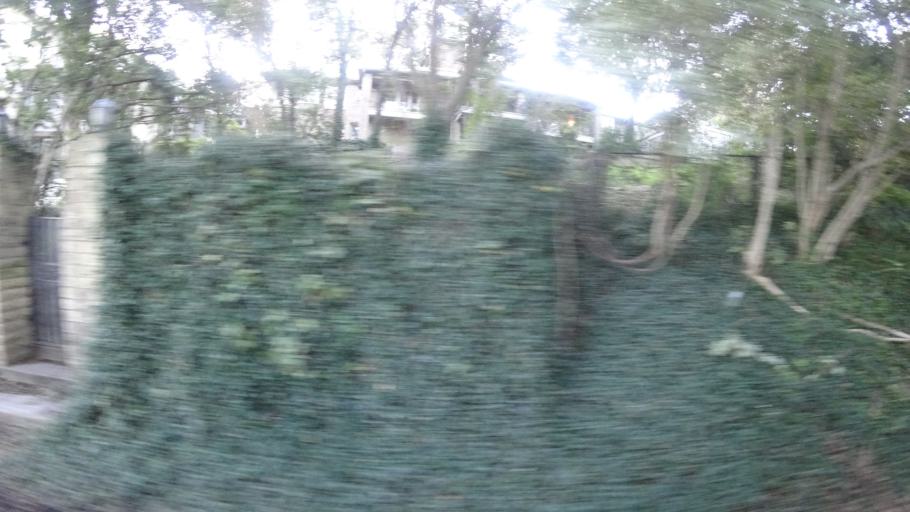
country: US
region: Texas
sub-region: Travis County
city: West Lake Hills
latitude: 30.3045
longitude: -97.7783
